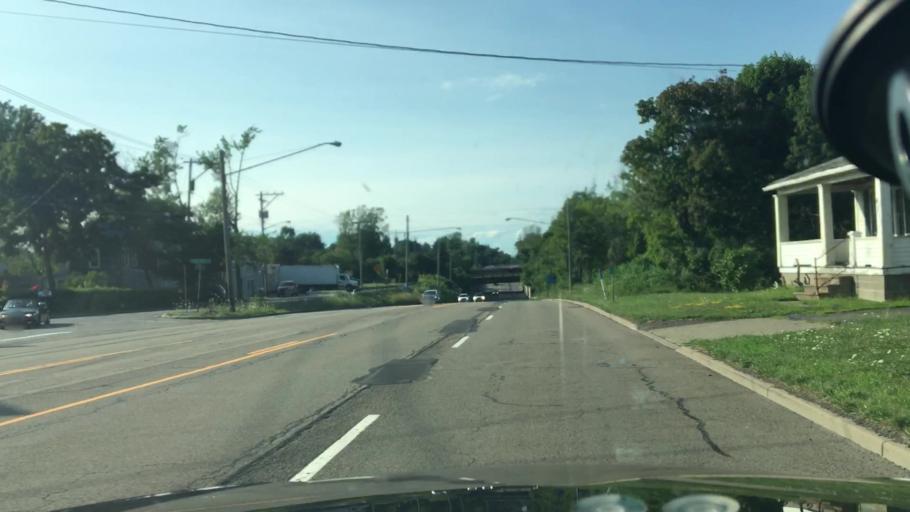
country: US
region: New York
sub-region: Erie County
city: Wanakah
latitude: 42.7626
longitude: -78.8630
